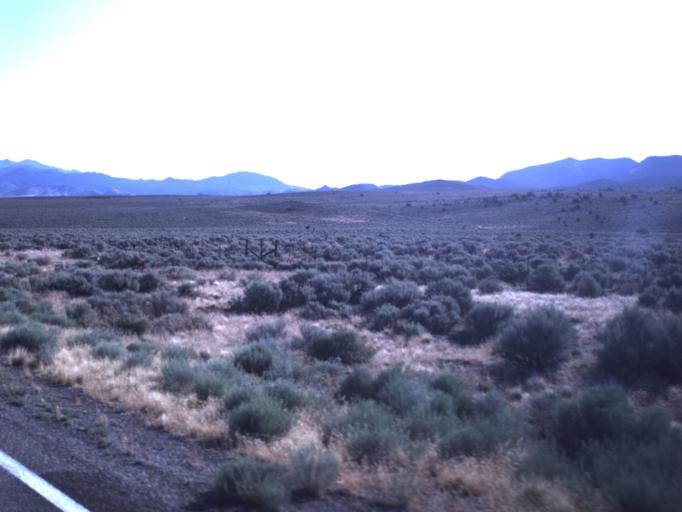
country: US
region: Utah
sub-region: Beaver County
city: Milford
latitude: 38.1513
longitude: -112.9594
